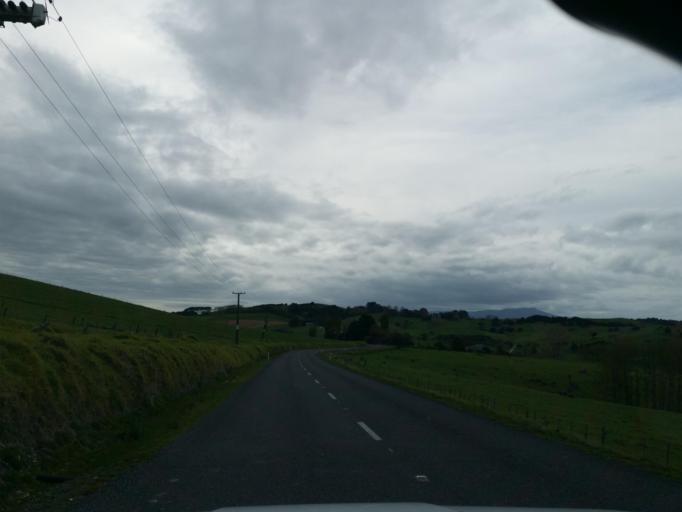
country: NZ
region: Northland
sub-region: Kaipara District
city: Dargaville
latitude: -35.9725
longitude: 173.9458
